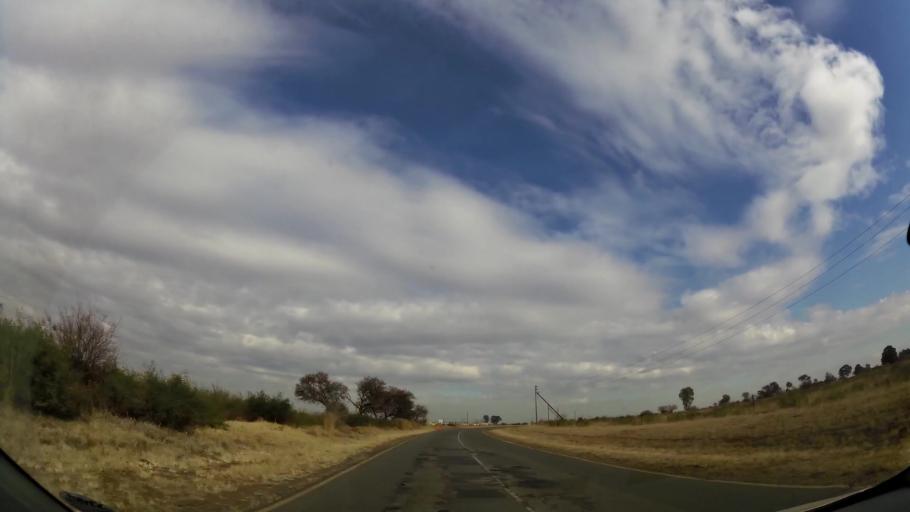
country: ZA
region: Gauteng
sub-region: Sedibeng District Municipality
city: Meyerton
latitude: -26.5582
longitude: 28.0583
